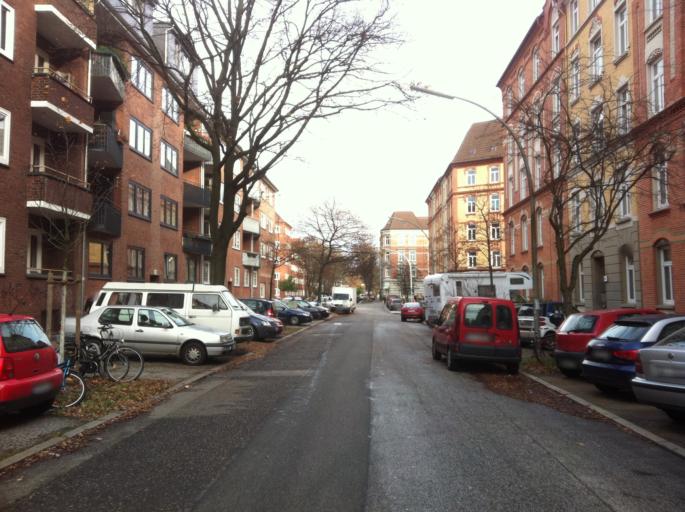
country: DE
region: Hamburg
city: Altona
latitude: 53.5576
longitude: 9.9394
